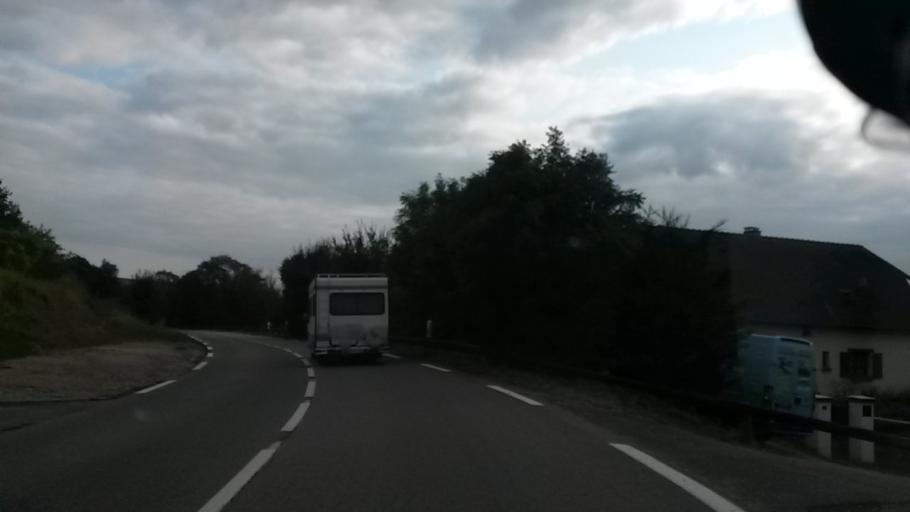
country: FR
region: Haute-Normandie
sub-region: Departement de l'Eure
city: Gravigny
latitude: 49.0662
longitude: 1.1745
